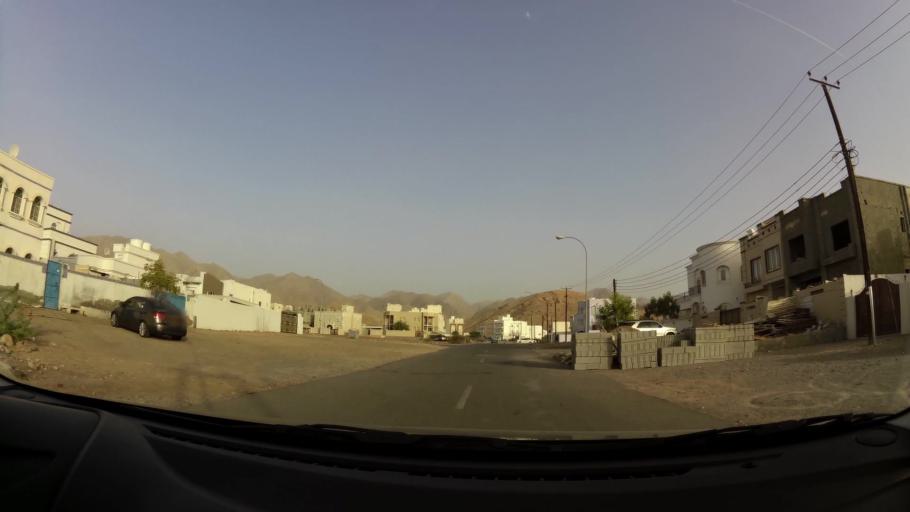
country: OM
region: Muhafazat Masqat
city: Bawshar
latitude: 23.5124
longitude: 58.3440
